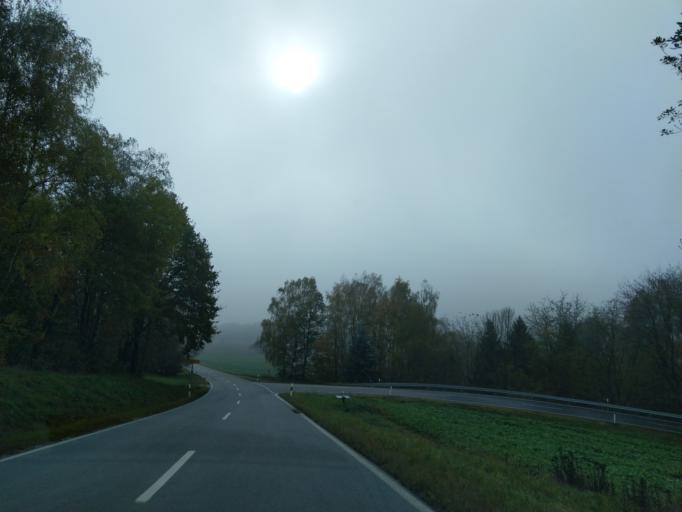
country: DE
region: Bavaria
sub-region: Lower Bavaria
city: Grattersdorf
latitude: 48.7907
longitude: 13.1582
